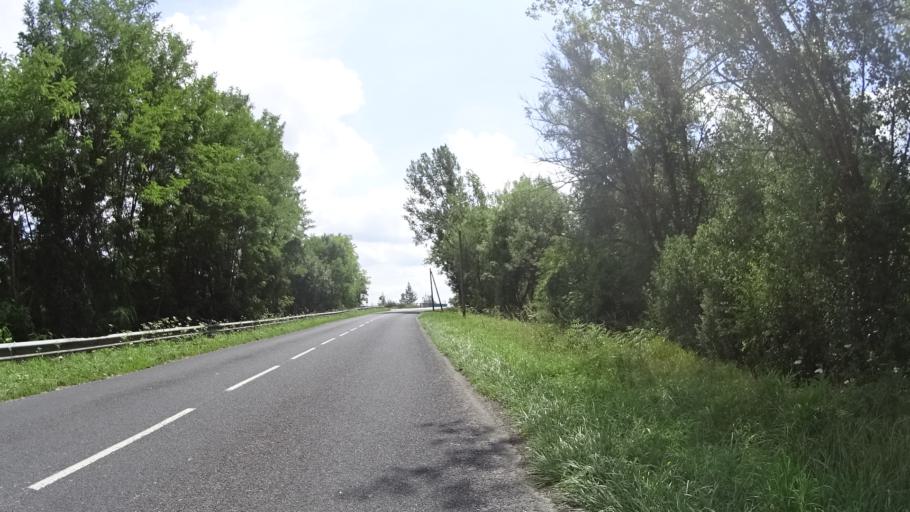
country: FR
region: Lorraine
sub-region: Departement de la Meuse
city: Euville
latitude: 48.7194
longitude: 5.6650
